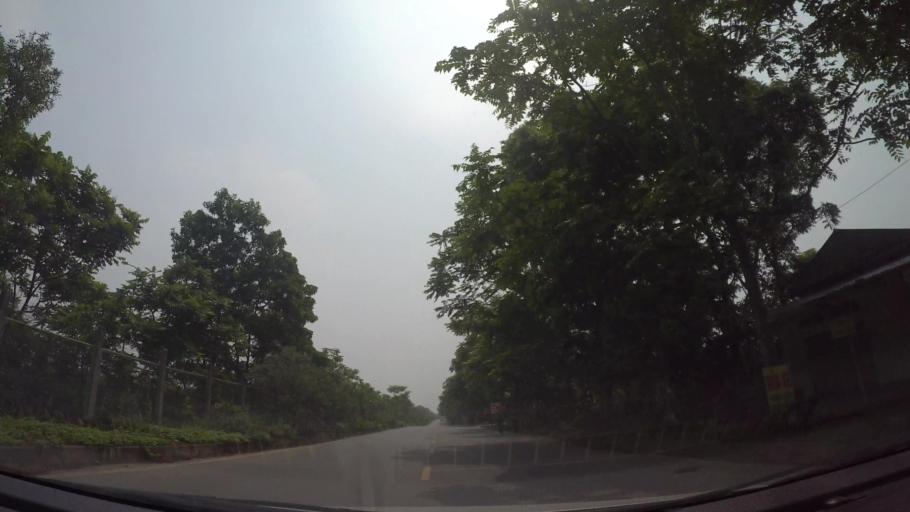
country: VN
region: Ha Noi
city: Lien Quan
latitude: 20.9900
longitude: 105.5447
